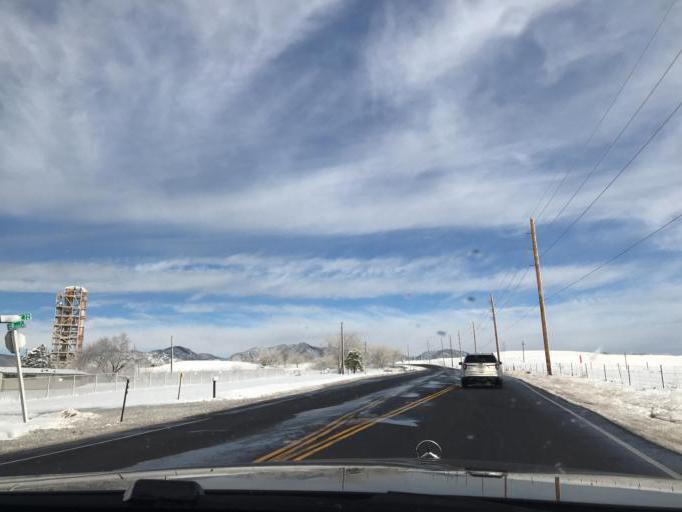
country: US
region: Colorado
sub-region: Boulder County
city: Superior
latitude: 39.8602
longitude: -105.1950
